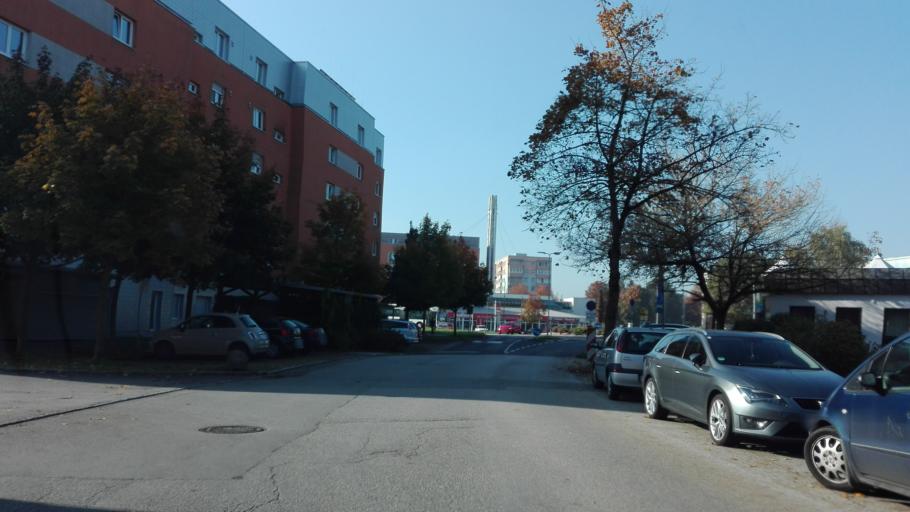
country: AT
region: Upper Austria
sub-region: Politischer Bezirk Linz-Land
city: Leonding
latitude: 48.2649
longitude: 14.2588
